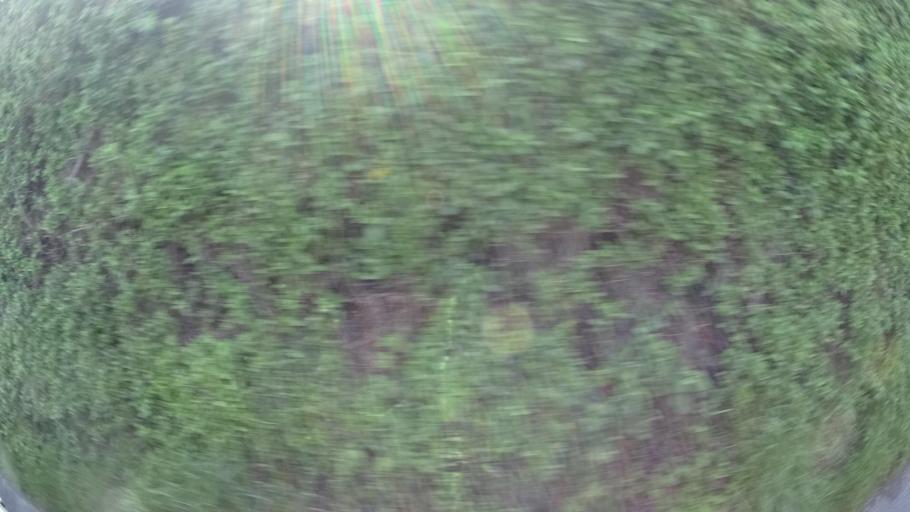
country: US
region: California
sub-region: Humboldt County
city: Humboldt Hill
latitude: 40.6726
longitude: -124.2166
